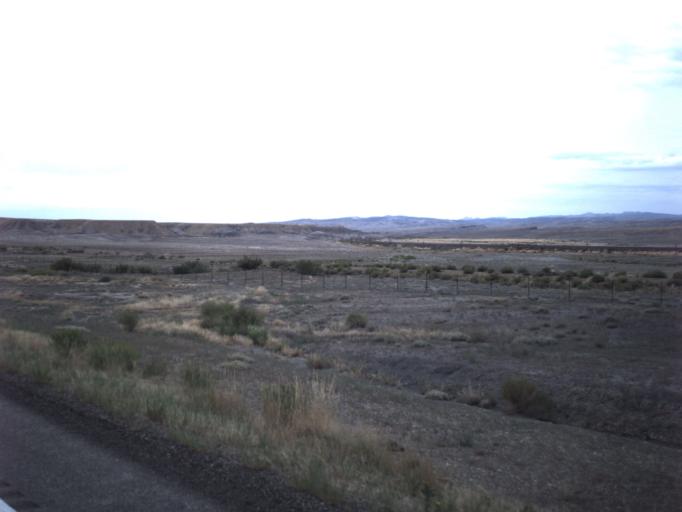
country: US
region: Utah
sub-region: Carbon County
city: East Carbon City
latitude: 39.3543
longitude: -110.3833
